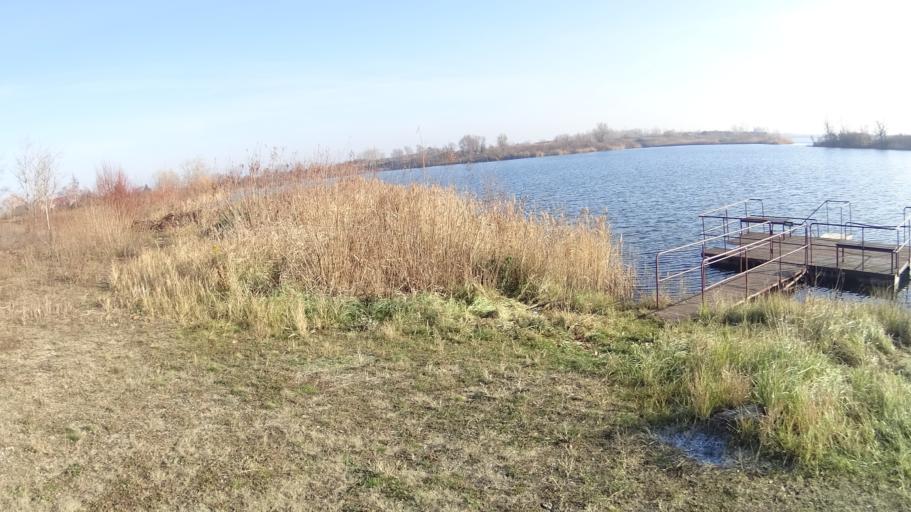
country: HU
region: Borsod-Abauj-Zemplen
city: Nyekladhaza
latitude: 47.9914
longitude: 20.8622
